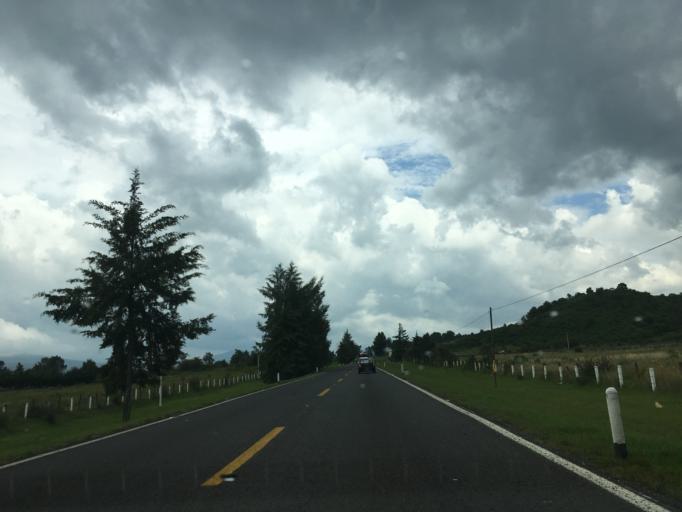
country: MX
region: Michoacan
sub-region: Patzcuaro
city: Santa Ana Chapitiro
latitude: 19.5274
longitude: -101.6436
